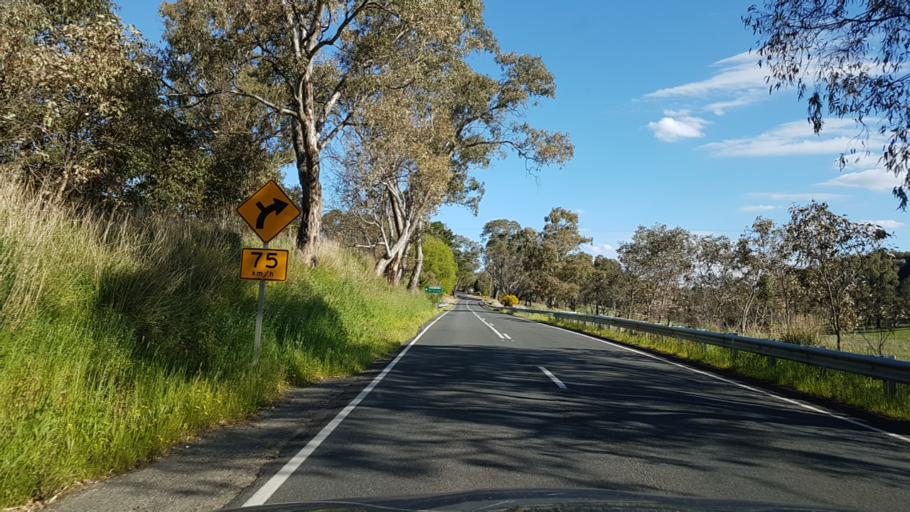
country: AU
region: South Australia
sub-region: Adelaide Hills
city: Gumeracha
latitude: -34.8523
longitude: 138.8936
